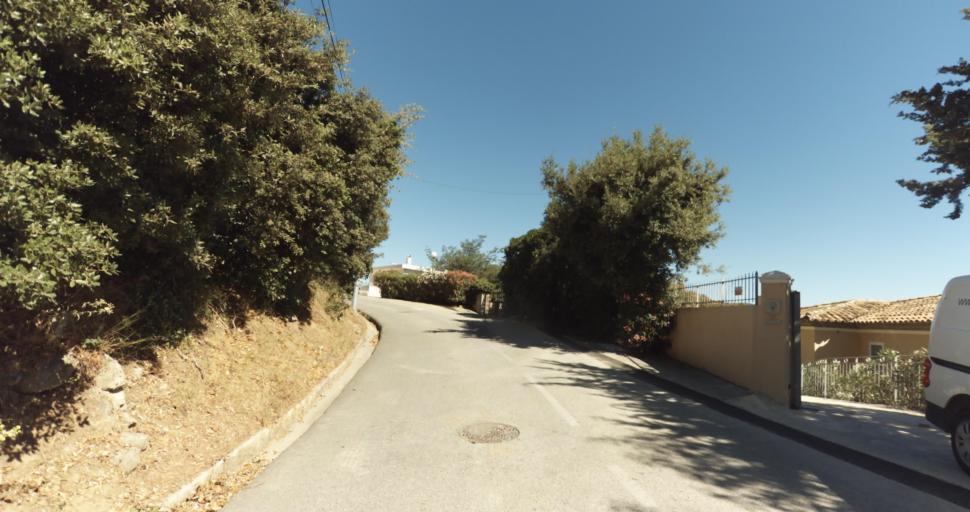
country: FR
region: Provence-Alpes-Cote d'Azur
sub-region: Departement du Var
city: Saint-Tropez
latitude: 43.2595
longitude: 6.6092
